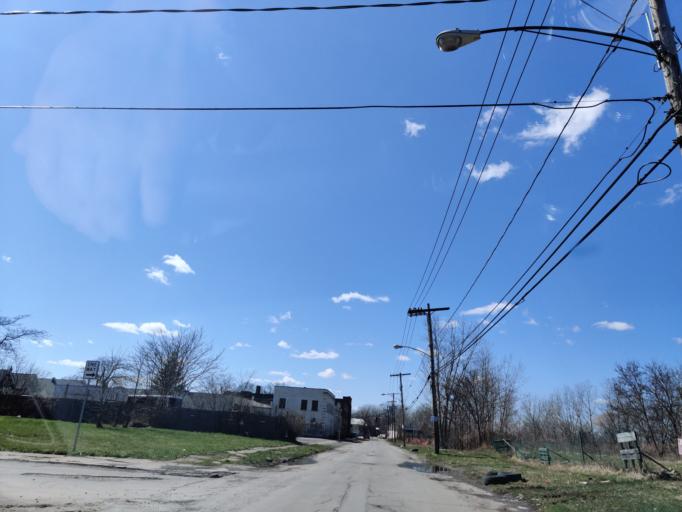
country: US
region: New York
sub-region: Erie County
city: Kenmore
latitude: 42.9433
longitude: -78.8883
